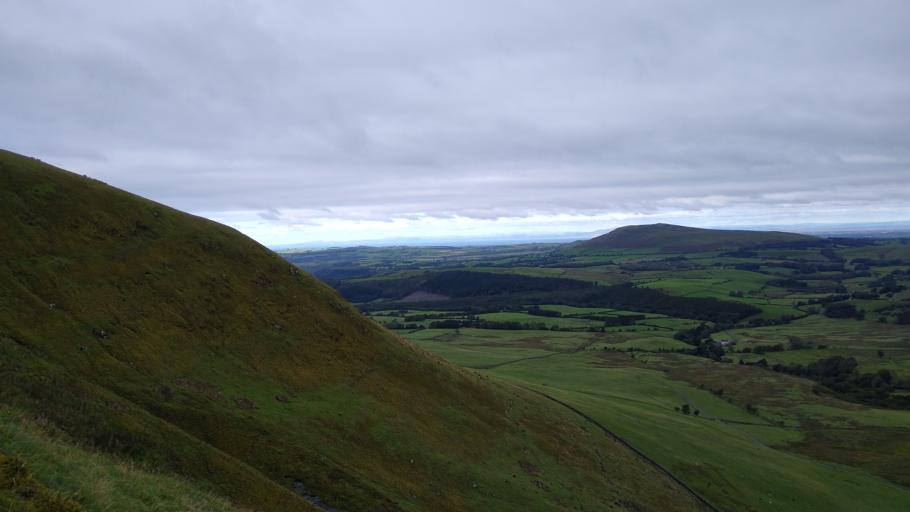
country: GB
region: England
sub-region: Cumbria
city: Keswick
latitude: 54.6740
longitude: -3.1432
